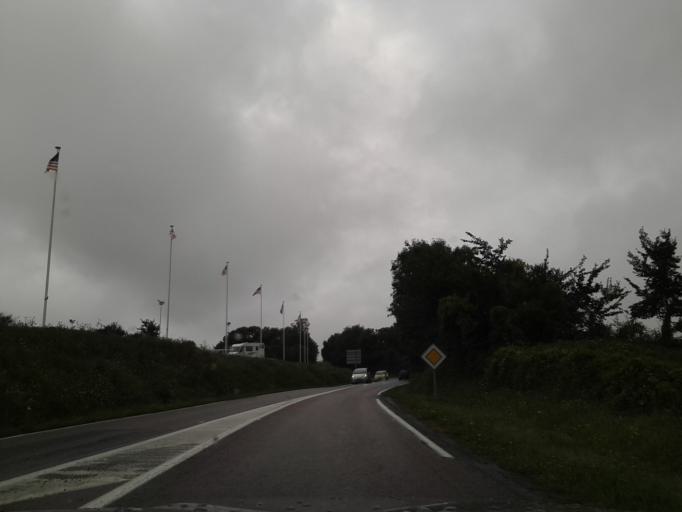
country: FR
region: Lower Normandy
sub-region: Departement de la Manche
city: Carentan
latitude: 49.3289
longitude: -1.2681
